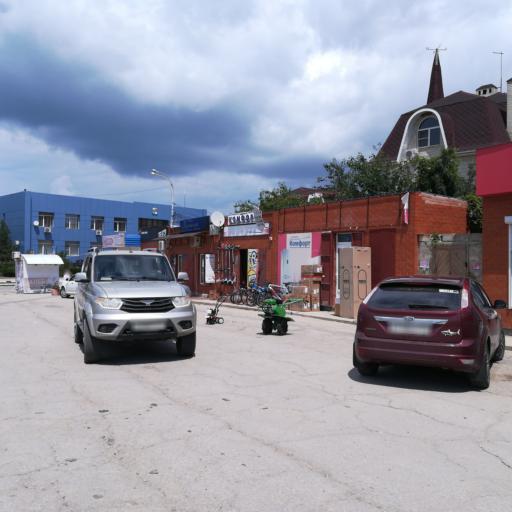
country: RU
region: Krasnodarskiy
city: Taman'
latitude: 45.2155
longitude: 36.7196
